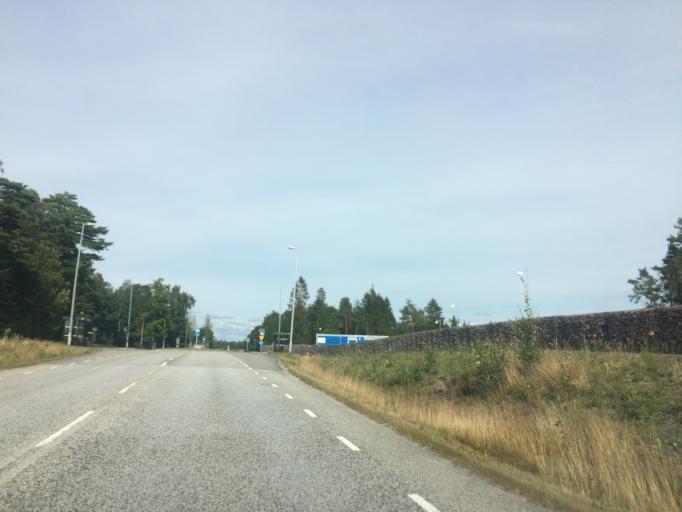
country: SE
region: Vaestra Goetaland
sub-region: Partille Kommun
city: Ojersjo
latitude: 57.6836
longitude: 12.0995
